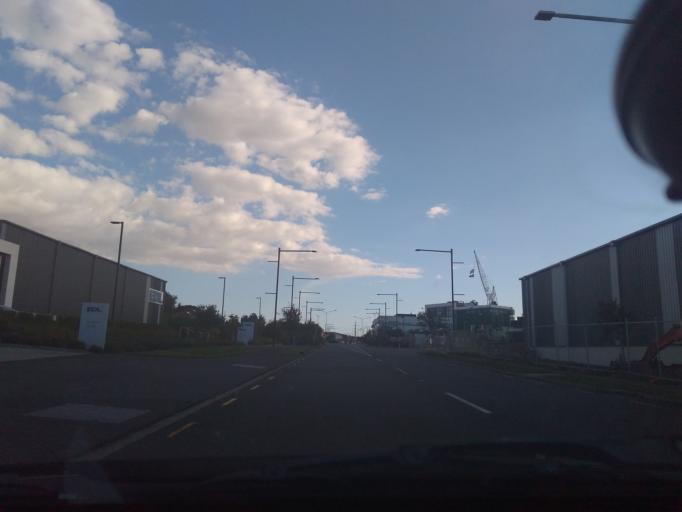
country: NZ
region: Auckland
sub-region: Auckland
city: Tamaki
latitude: -36.9346
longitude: 174.8765
